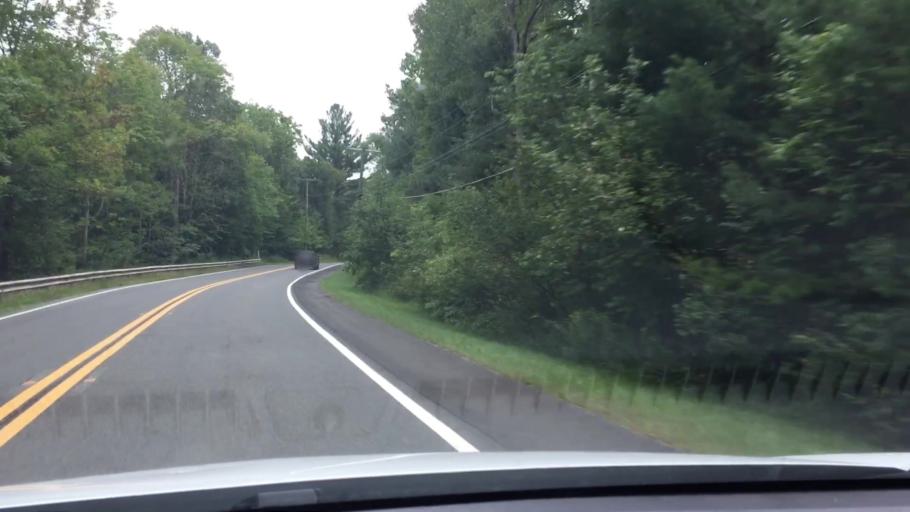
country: US
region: Massachusetts
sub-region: Berkshire County
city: Hinsdale
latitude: 42.3800
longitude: -73.1216
